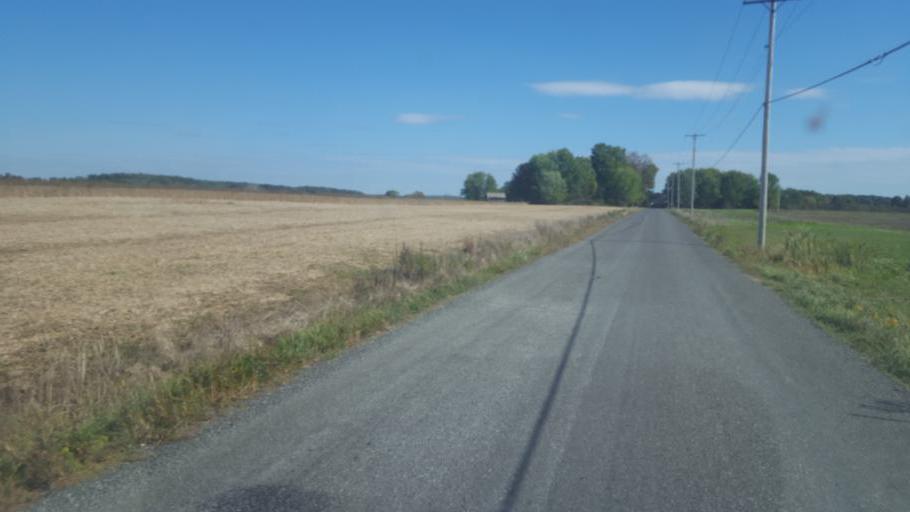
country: US
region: Pennsylvania
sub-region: Mercer County
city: Reynolds Heights
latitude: 41.3287
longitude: -80.2964
